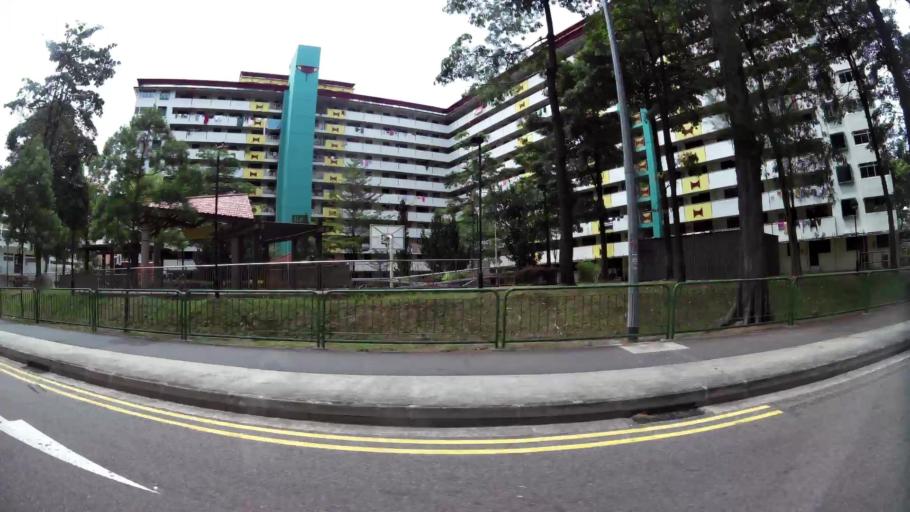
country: SG
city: Singapore
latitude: 1.3351
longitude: 103.7250
